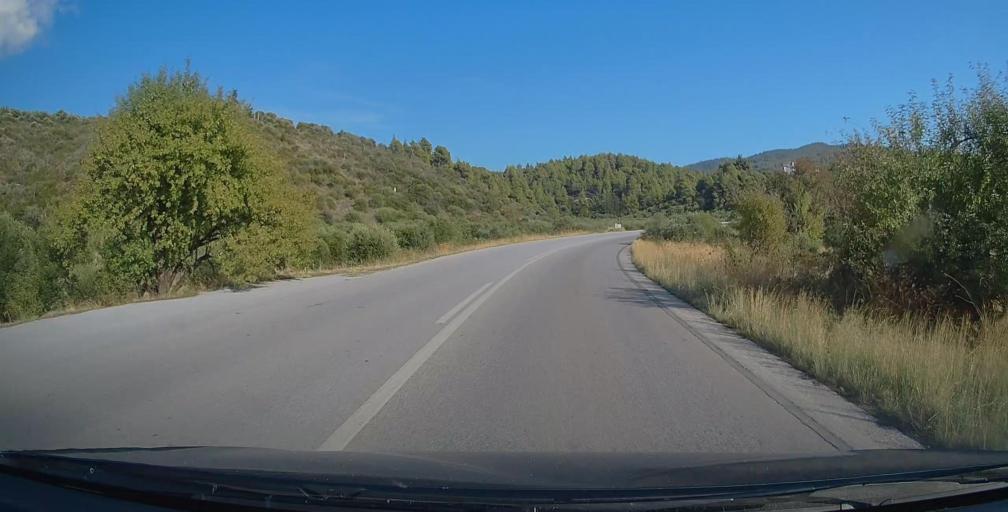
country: GR
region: Central Macedonia
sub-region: Nomos Chalkidikis
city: Neos Marmaras
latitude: 40.0852
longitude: 23.8075
